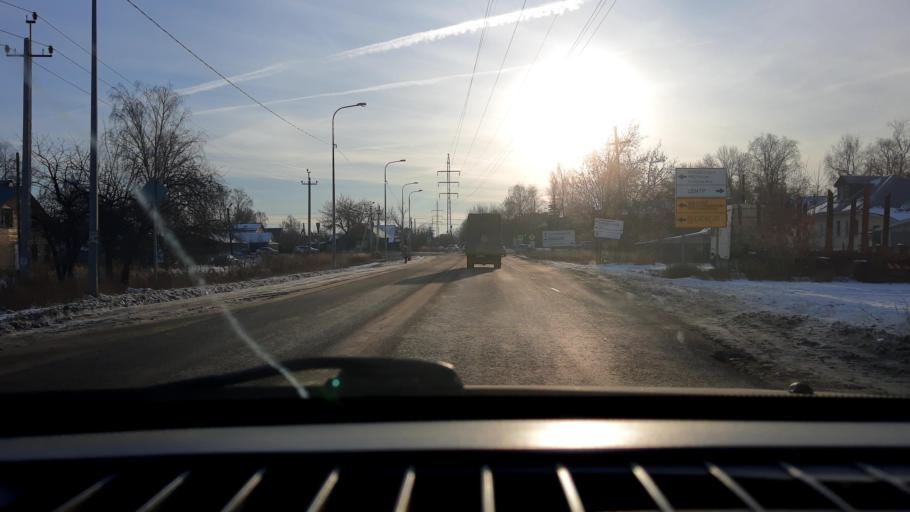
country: RU
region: Nizjnij Novgorod
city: Bor
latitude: 56.3655
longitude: 44.0714
